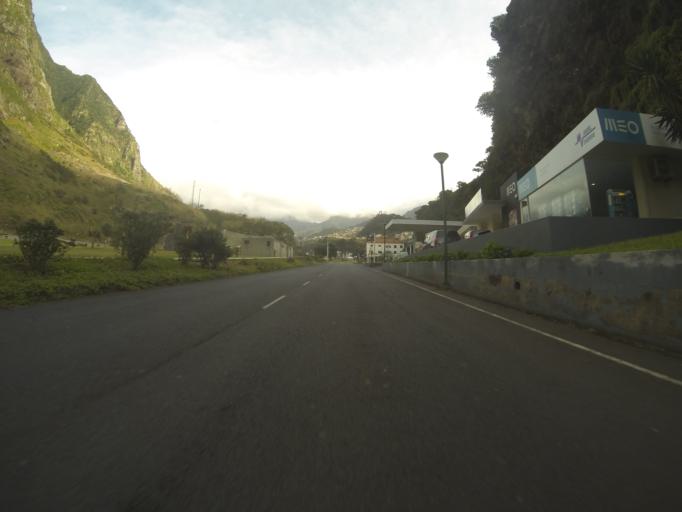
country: PT
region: Madeira
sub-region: Sao Vicente
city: Sao Vicente
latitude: 32.8062
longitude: -17.0468
